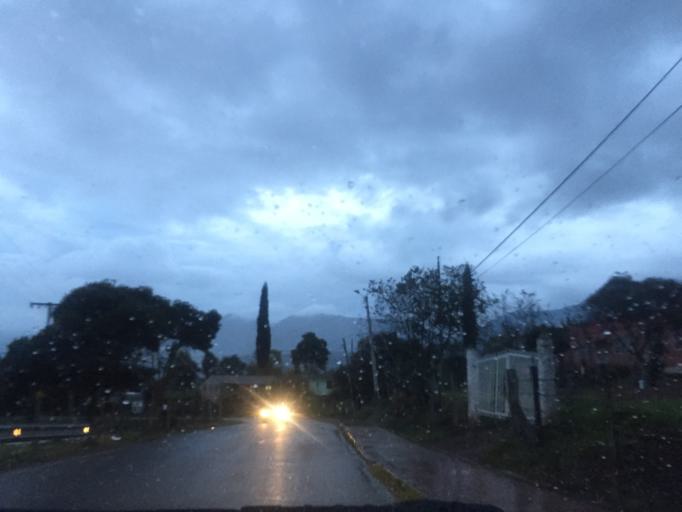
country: CO
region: Cundinamarca
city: Cogua
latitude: 5.0700
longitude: -73.9709
